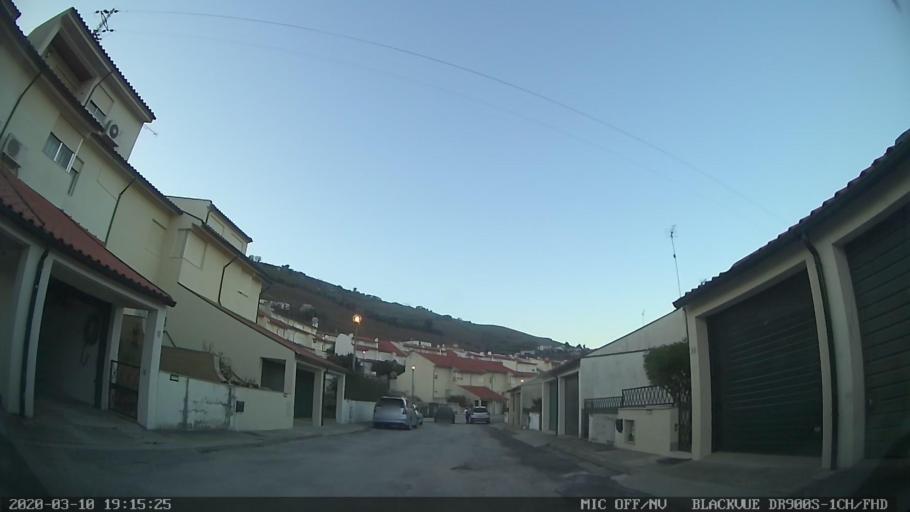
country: PT
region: Vila Real
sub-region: Peso da Regua
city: Godim
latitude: 41.1685
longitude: -7.8061
